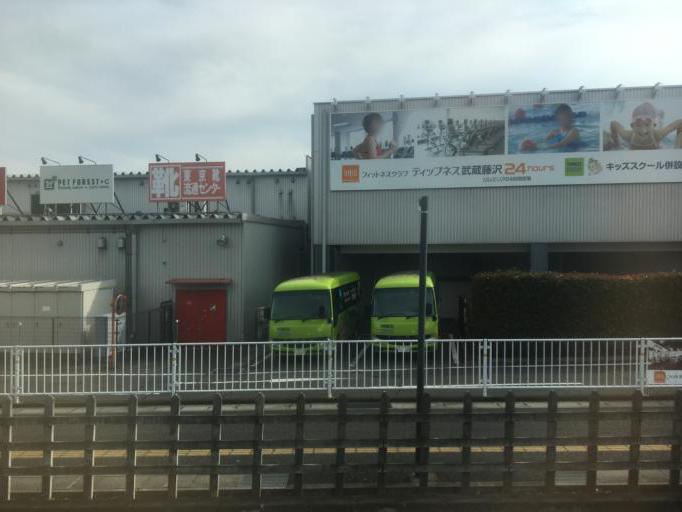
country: JP
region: Saitama
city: Sayama
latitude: 35.8197
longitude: 139.4129
